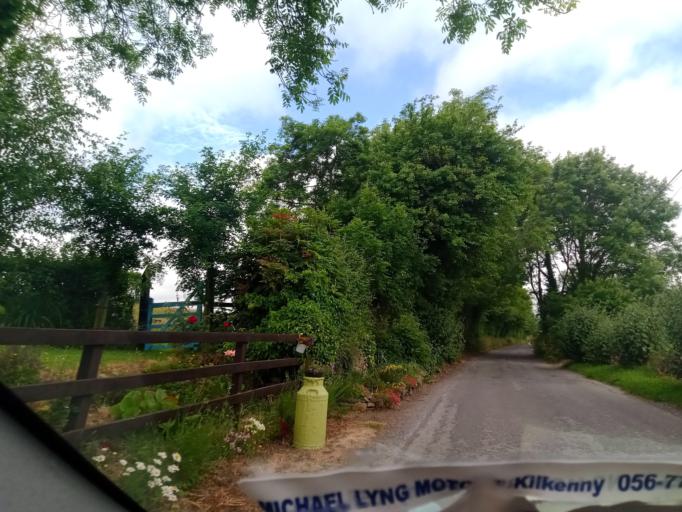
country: IE
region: Leinster
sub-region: Kilkenny
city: Ballyragget
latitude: 52.7592
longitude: -7.4529
